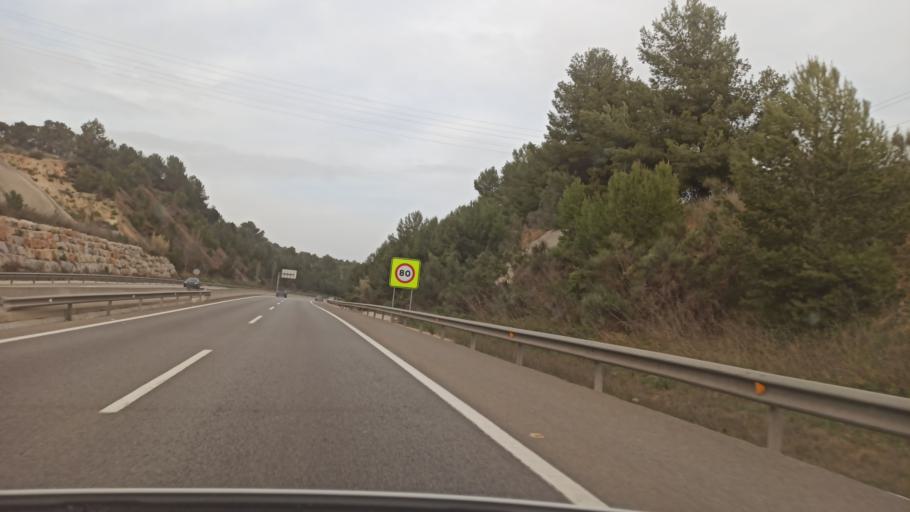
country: ES
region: Catalonia
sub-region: Provincia de Barcelona
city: Palleja
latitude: 41.4092
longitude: 1.9902
